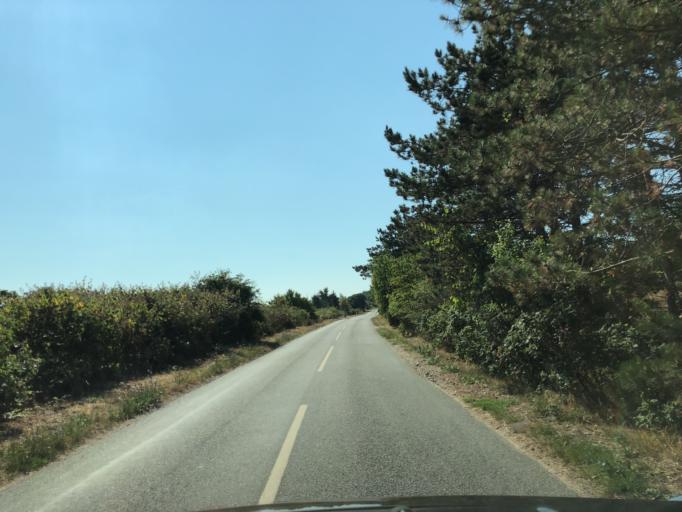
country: DK
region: Zealand
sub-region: Odsherred Kommune
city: Asnaes
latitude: 55.9913
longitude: 11.2952
